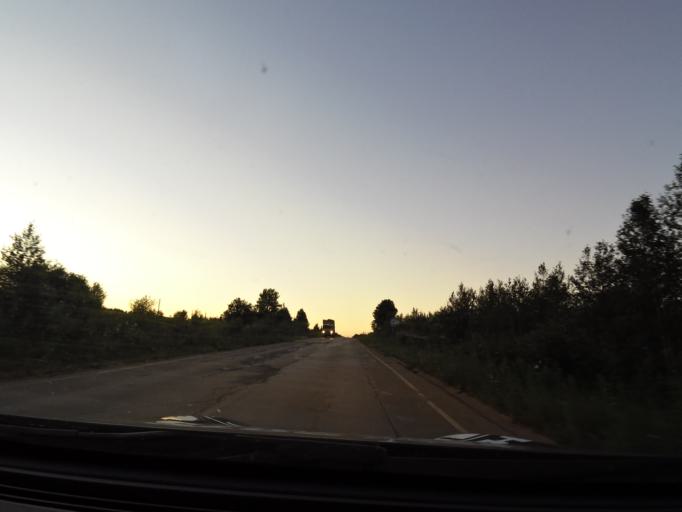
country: RU
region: Vologda
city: Vytegra
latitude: 60.8813
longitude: 36.0371
